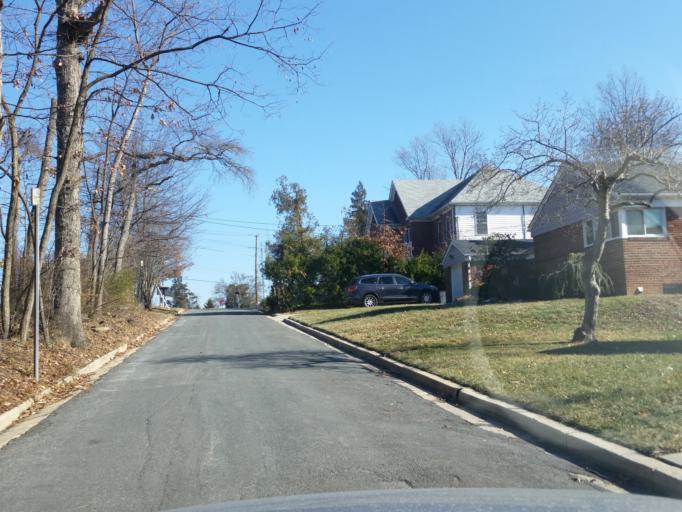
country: US
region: Maryland
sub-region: Montgomery County
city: Forest Glen
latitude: 38.9932
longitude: -77.0529
